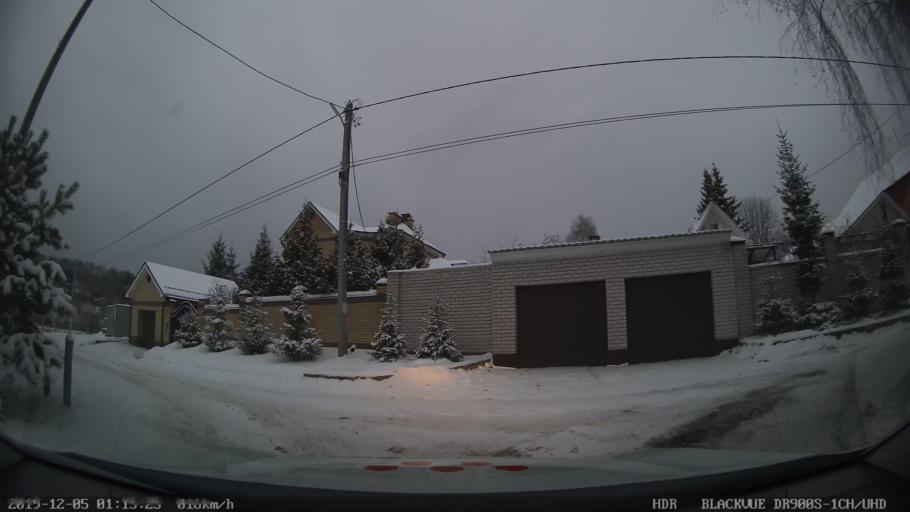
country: RU
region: Tatarstan
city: Stolbishchi
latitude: 55.6457
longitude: 49.1128
